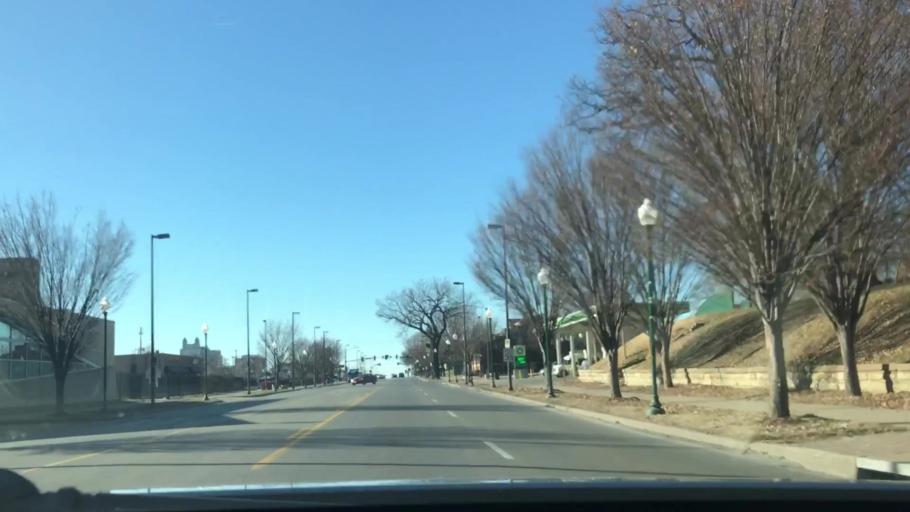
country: US
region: Missouri
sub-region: Jackson County
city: Kansas City
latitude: 39.1066
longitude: -94.5572
